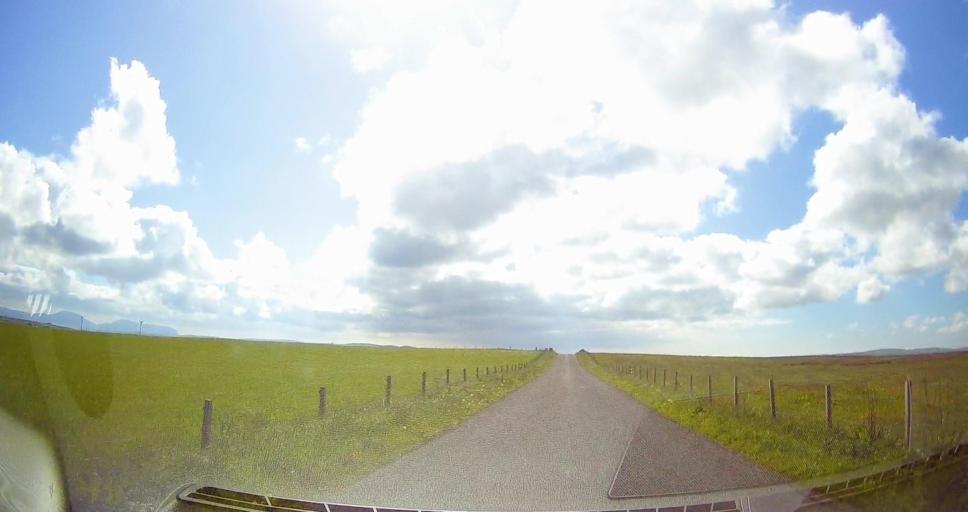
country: GB
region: Scotland
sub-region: Orkney Islands
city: Stromness
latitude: 59.0458
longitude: -3.1615
